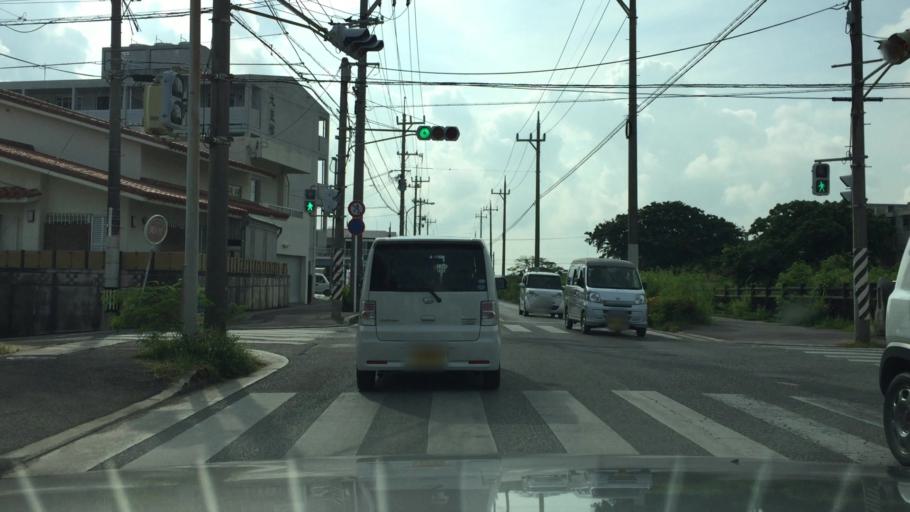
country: JP
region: Okinawa
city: Ishigaki
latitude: 24.3488
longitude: 124.1656
